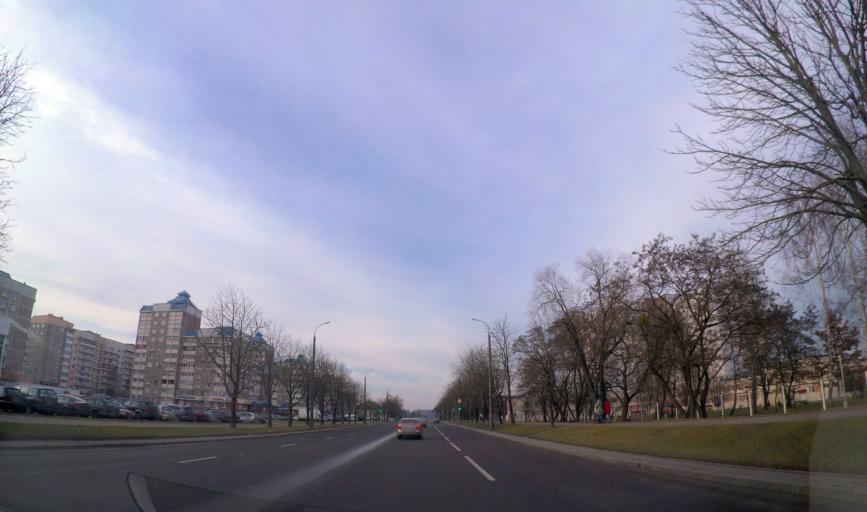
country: BY
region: Grodnenskaya
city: Hrodna
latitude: 53.6724
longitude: 23.7990
